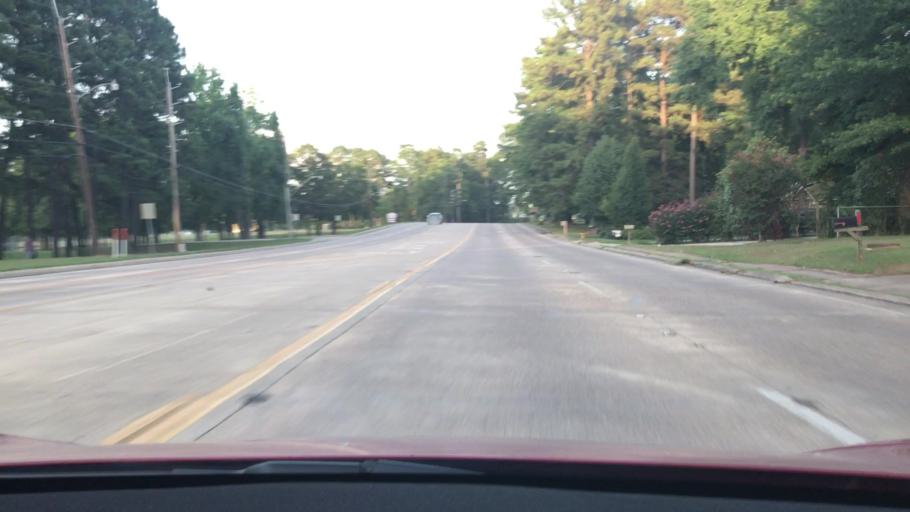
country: US
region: Louisiana
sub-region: De Soto Parish
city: Stonewall
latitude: 32.4020
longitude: -93.7871
